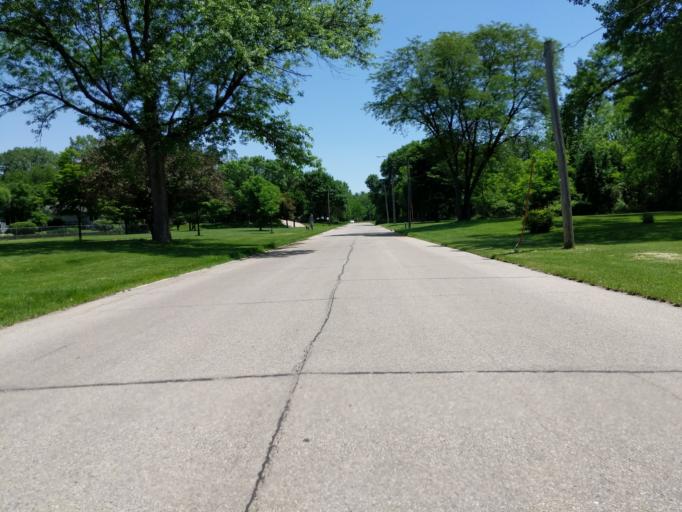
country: US
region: Iowa
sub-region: Linn County
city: Cedar Rapids
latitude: 42.0178
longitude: -91.6273
